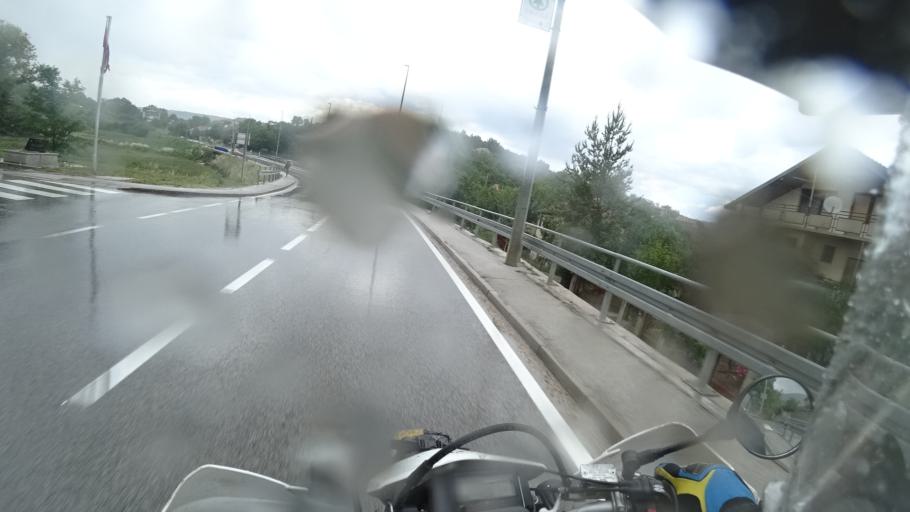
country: HR
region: Sibensko-Kniniska
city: Knin
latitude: 44.0448
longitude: 16.2151
